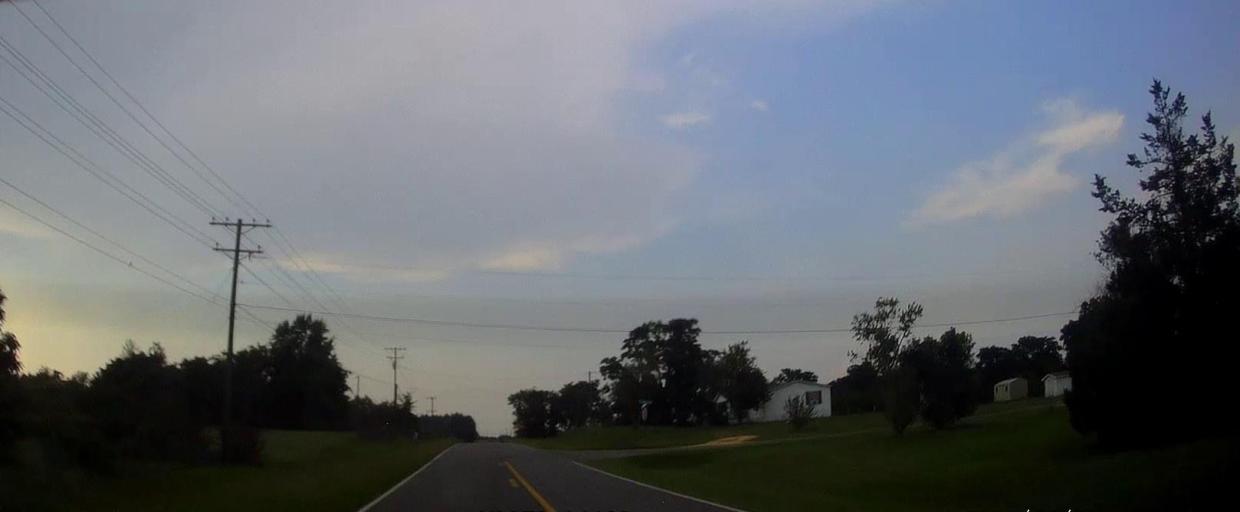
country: US
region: Georgia
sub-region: Laurens County
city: East Dublin
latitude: 32.5514
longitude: -82.8375
